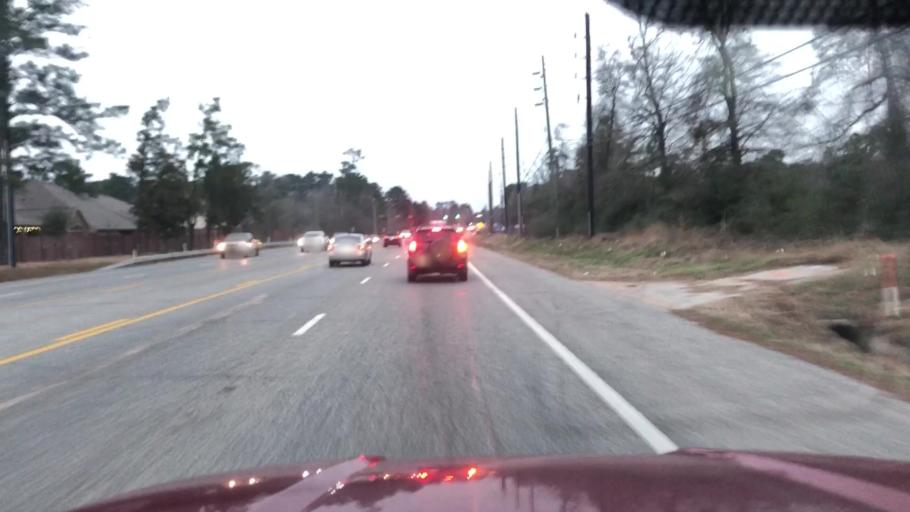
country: US
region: Texas
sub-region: Harris County
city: Tomball
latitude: 30.0802
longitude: -95.5625
